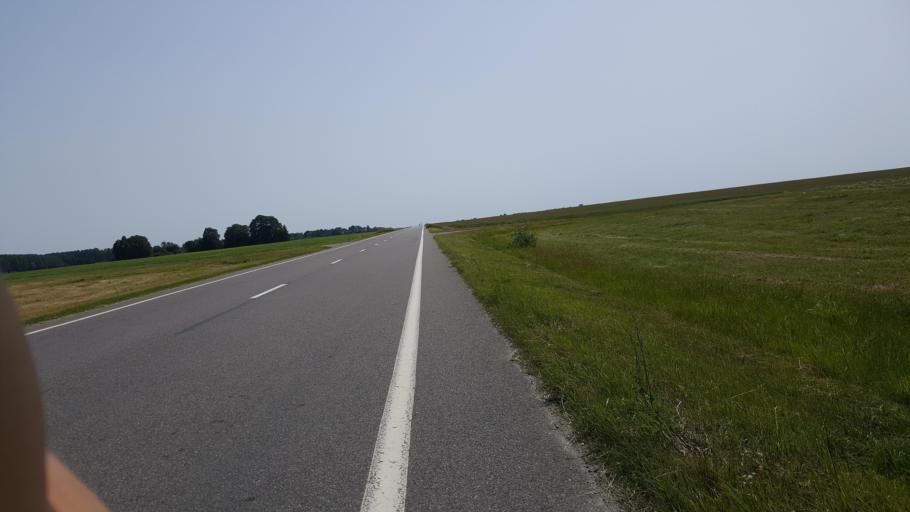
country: BY
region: Brest
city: Kamyanyets
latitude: 52.4496
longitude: 23.8336
